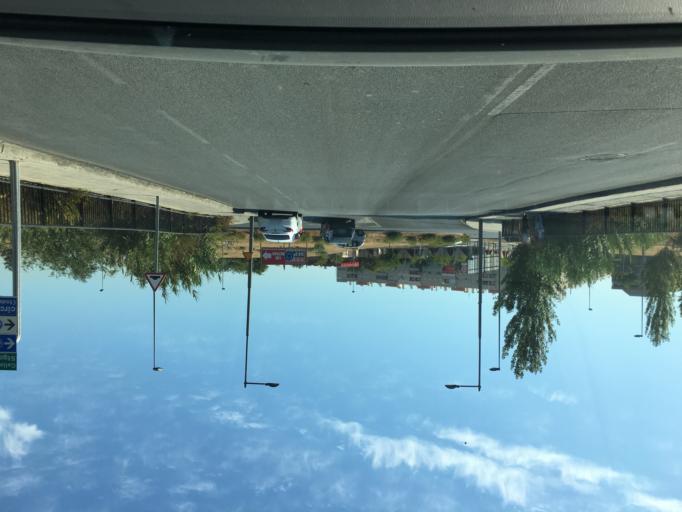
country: ES
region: Andalusia
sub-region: Provincia de Granada
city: Maracena
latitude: 37.2107
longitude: -3.6201
